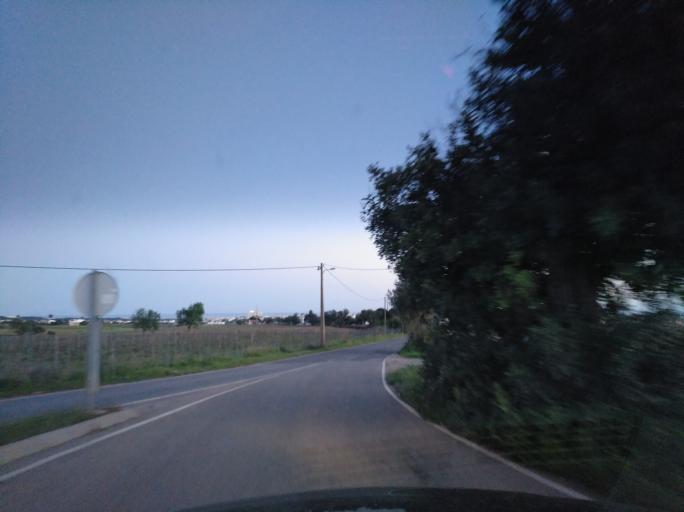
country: PT
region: Faro
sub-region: Vila Real de Santo Antonio
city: Monte Gordo
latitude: 37.1929
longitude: -7.5138
